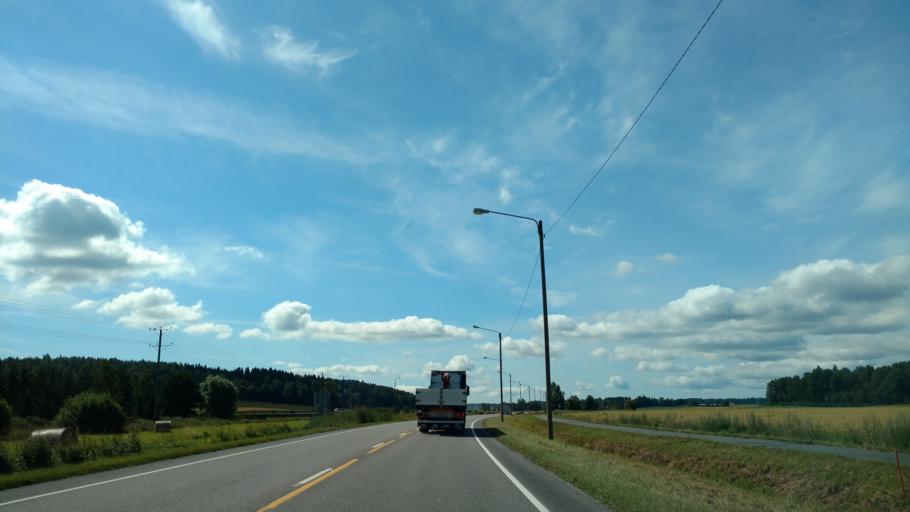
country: FI
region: Varsinais-Suomi
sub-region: Salo
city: Pernioe
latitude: 60.2523
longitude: 23.1348
